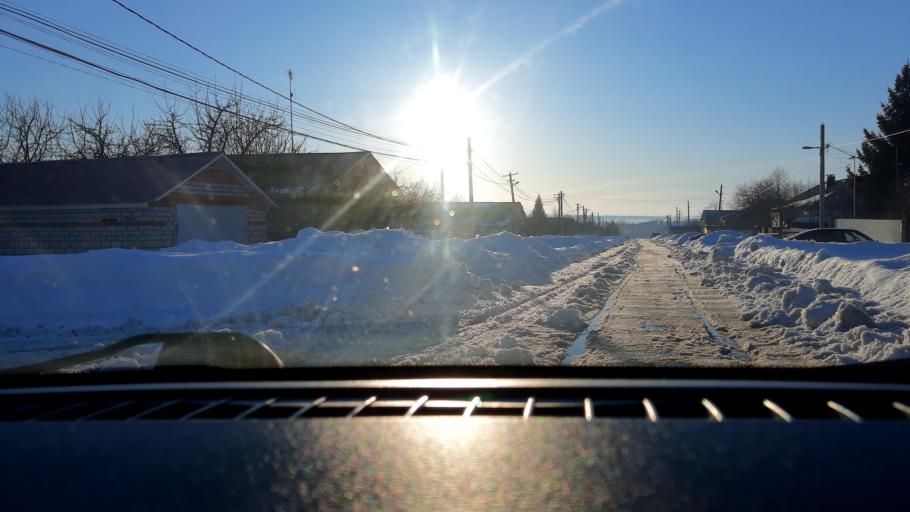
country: RU
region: Bashkortostan
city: Avdon
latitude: 54.8174
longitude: 55.7122
